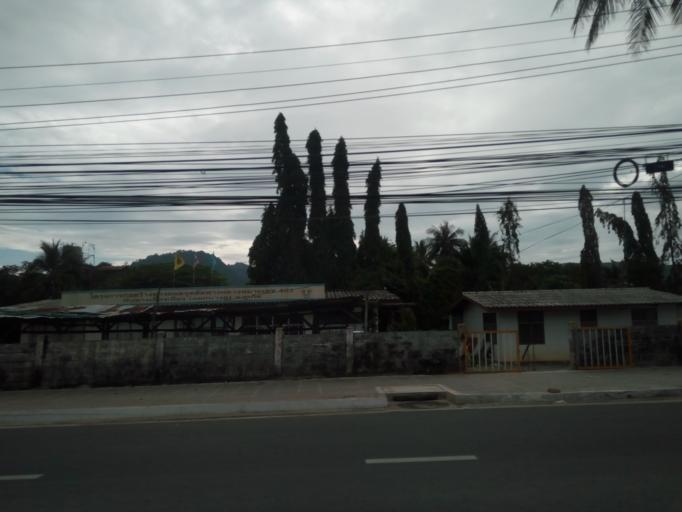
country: TH
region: Phuket
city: Ban Ko Kaeo
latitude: 7.9597
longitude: 98.3829
